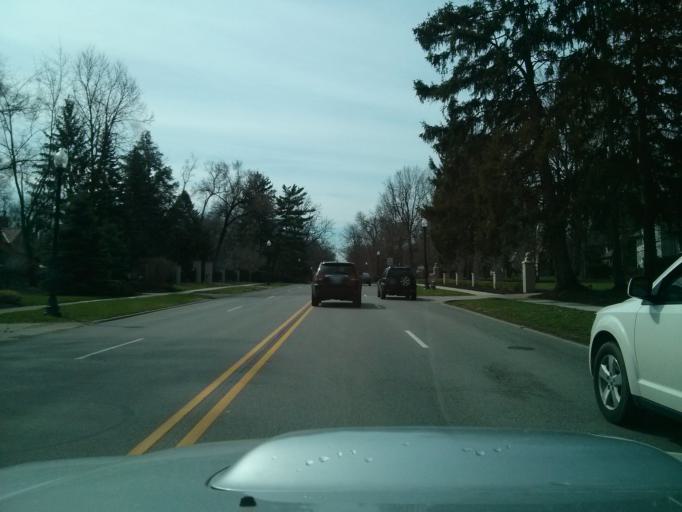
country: US
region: Indiana
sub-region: Marion County
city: Broad Ripple
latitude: 39.8460
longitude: -86.1571
